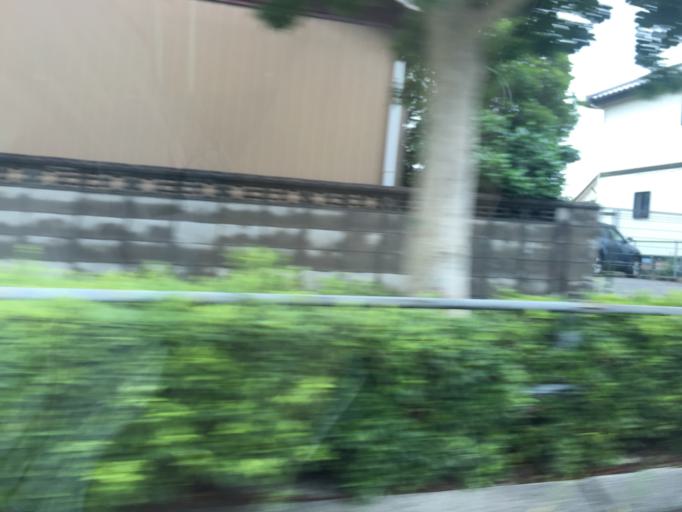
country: JP
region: Aichi
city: Ishiki
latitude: 34.8149
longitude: 137.0259
